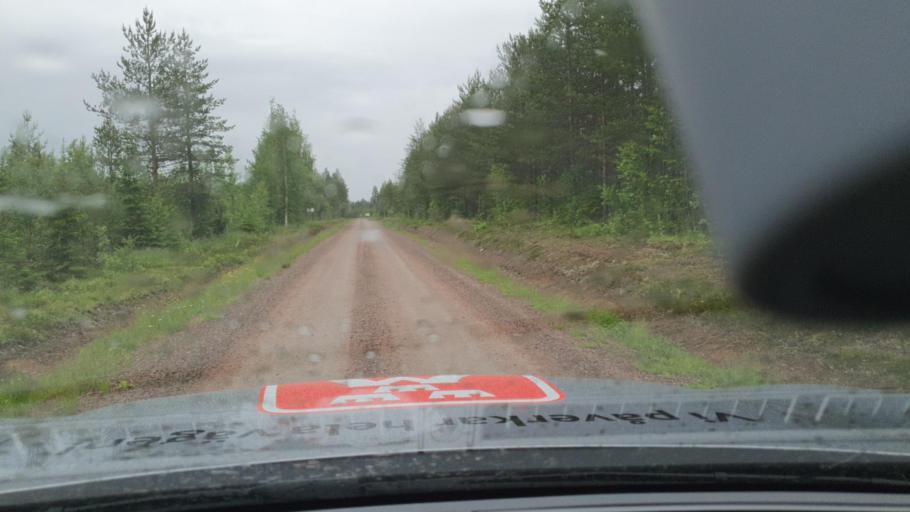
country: SE
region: Norrbotten
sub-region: Overkalix Kommun
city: OEverkalix
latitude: 66.5380
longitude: 22.7413
